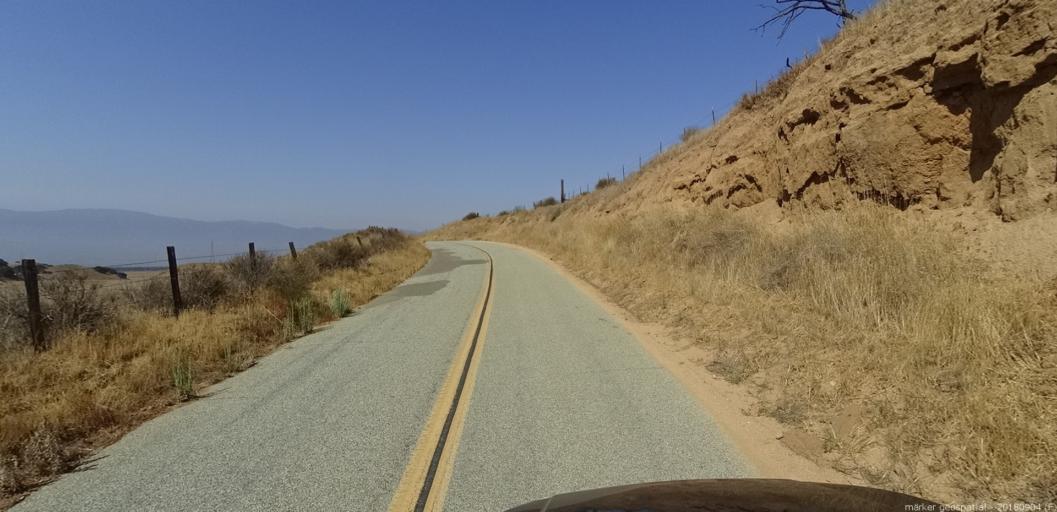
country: US
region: California
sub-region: Monterey County
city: Soledad
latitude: 36.5131
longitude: -121.3491
